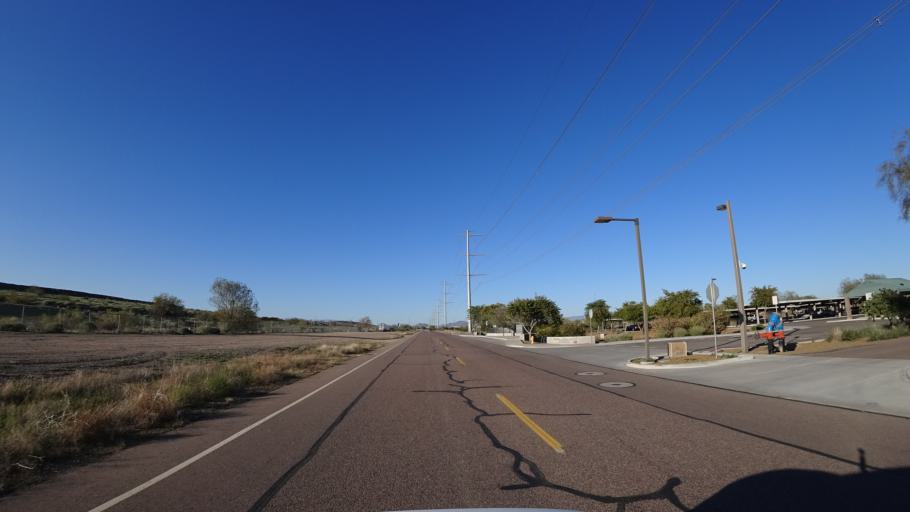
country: US
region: Arizona
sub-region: Maricopa County
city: Anthem
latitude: 33.7100
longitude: -112.1220
